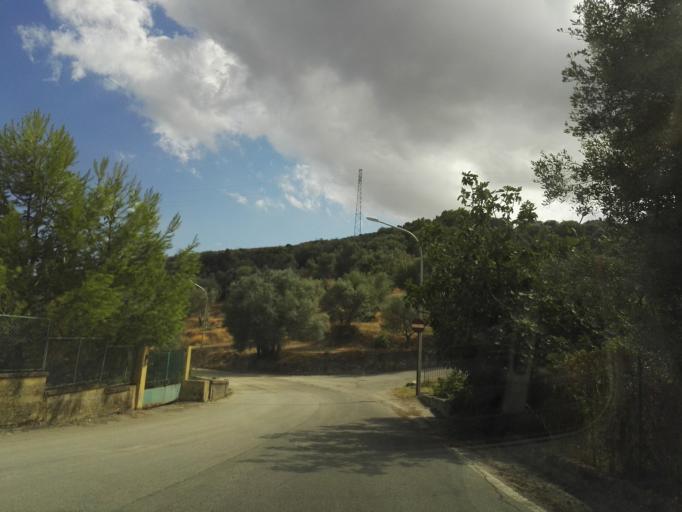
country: IT
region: Calabria
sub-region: Provincia di Reggio Calabria
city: Camini
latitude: 38.4299
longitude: 16.4859
